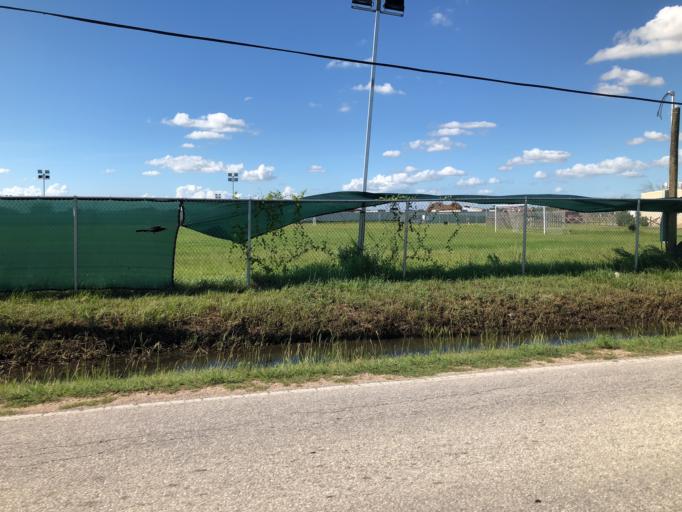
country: US
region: Texas
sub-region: Harris County
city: Katy
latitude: 29.8312
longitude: -95.8229
